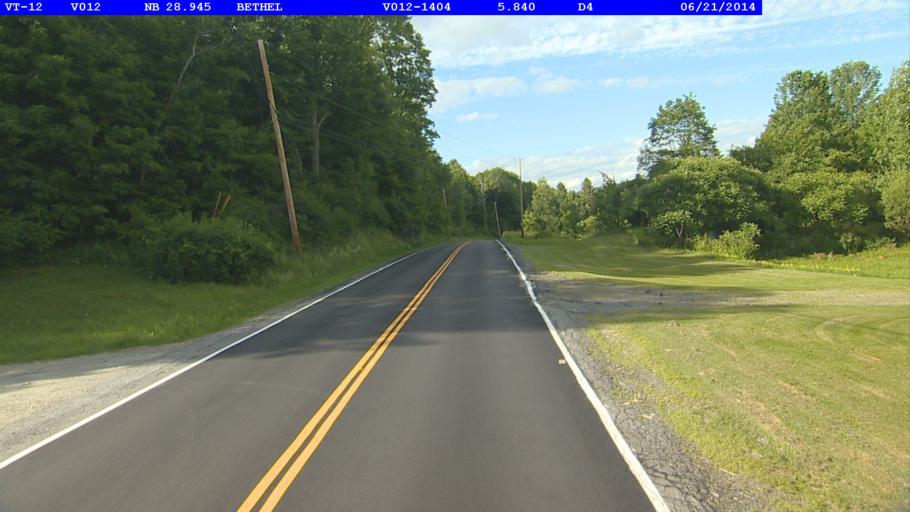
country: US
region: Vermont
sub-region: Orange County
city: Randolph
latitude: 43.8798
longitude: -72.6466
